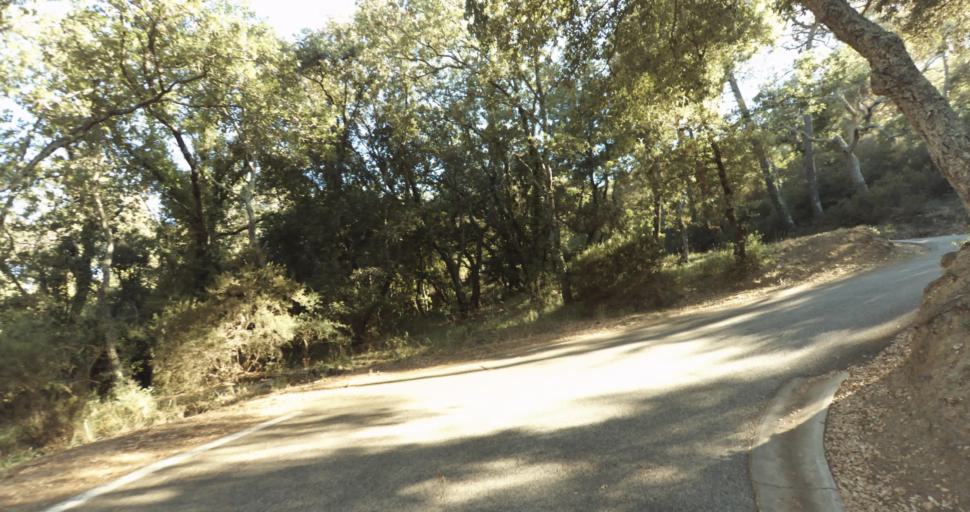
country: FR
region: Provence-Alpes-Cote d'Azur
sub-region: Departement du Var
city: Gassin
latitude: 43.2306
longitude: 6.5883
